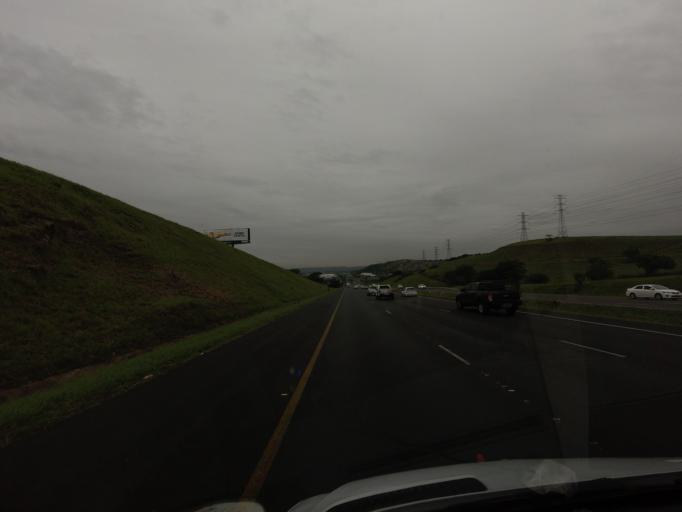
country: ZA
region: KwaZulu-Natal
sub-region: eThekwini Metropolitan Municipality
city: Berea
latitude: -29.7521
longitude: 31.0238
